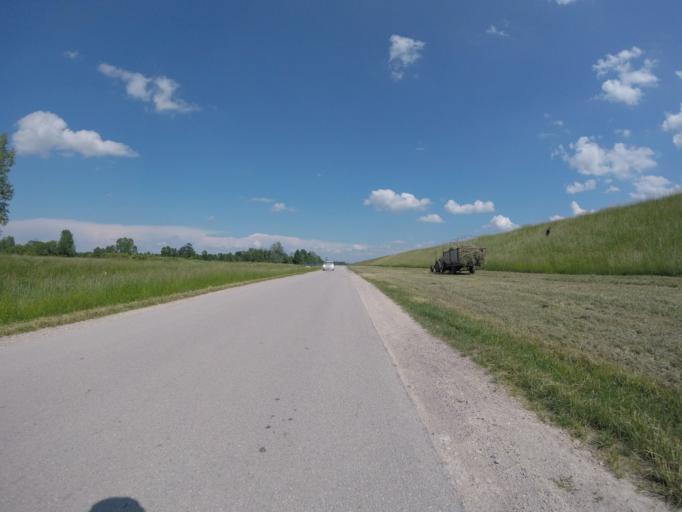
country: HR
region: Zagrebacka
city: Kuce
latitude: 45.6691
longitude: 16.1823
